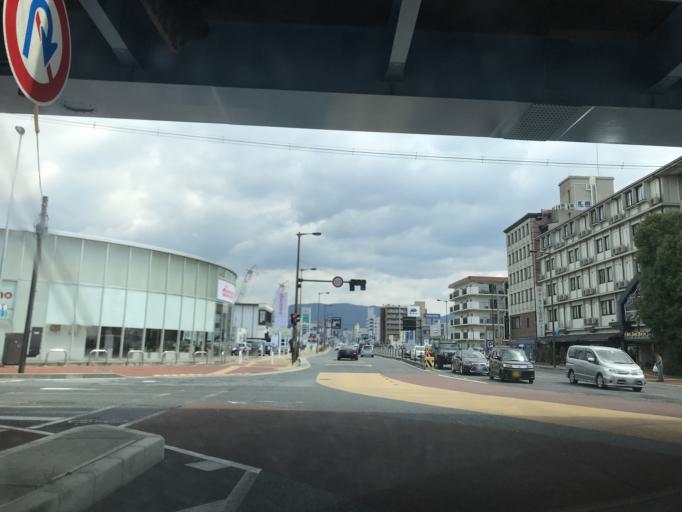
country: JP
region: Nara
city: Nara-shi
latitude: 34.6819
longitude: 135.8003
